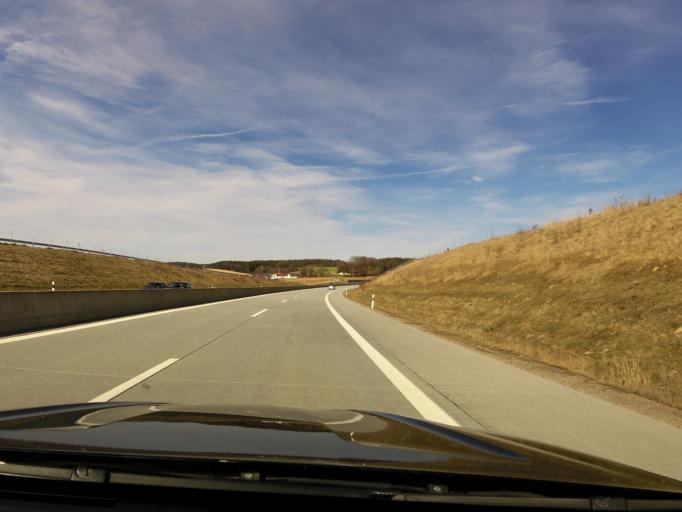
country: DE
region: Bavaria
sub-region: Upper Palatinate
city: Schierling
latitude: 48.7515
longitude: 12.1356
